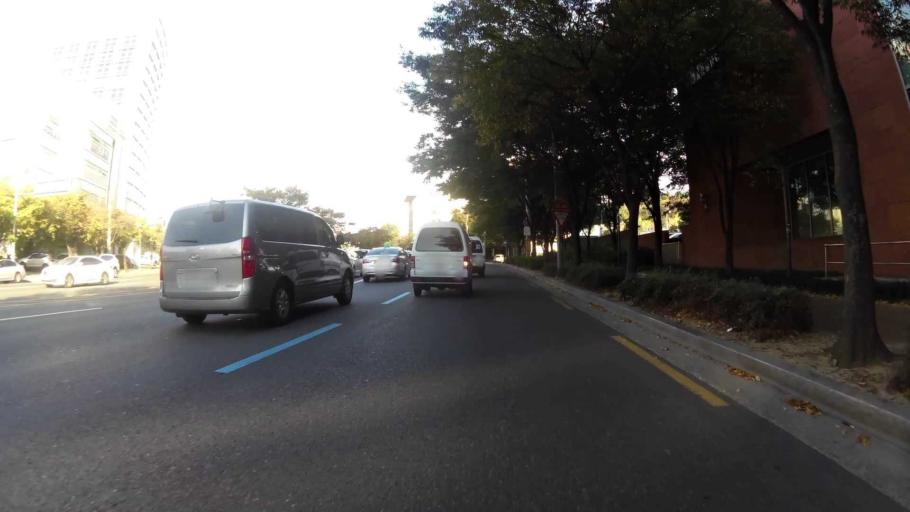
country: KR
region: Daegu
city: Daegu
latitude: 35.8665
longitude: 128.6288
